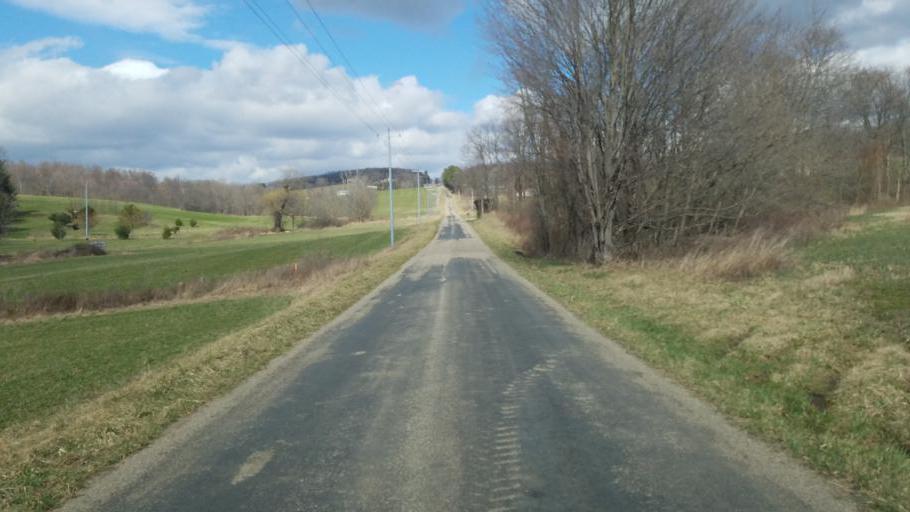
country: US
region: Ohio
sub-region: Sandusky County
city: Bellville
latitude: 40.5662
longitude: -82.4848
